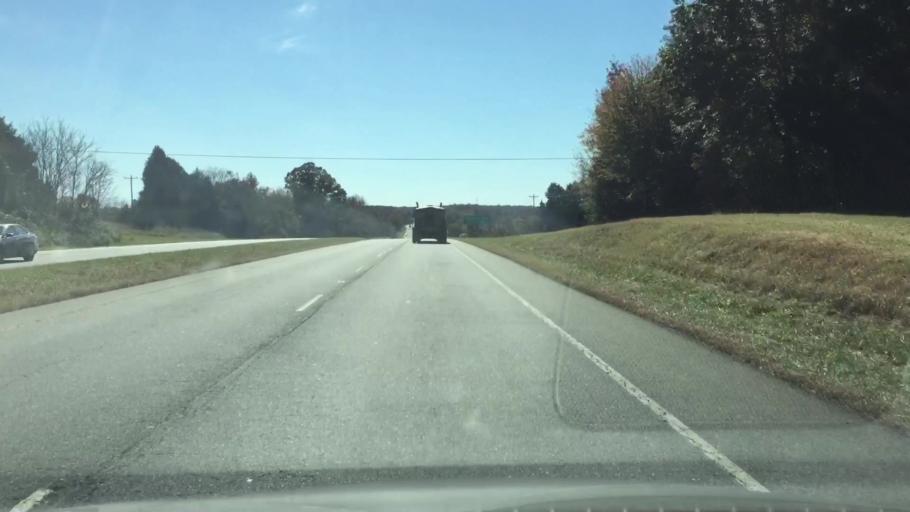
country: US
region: North Carolina
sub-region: Guilford County
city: McLeansville
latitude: 36.1881
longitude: -79.7043
